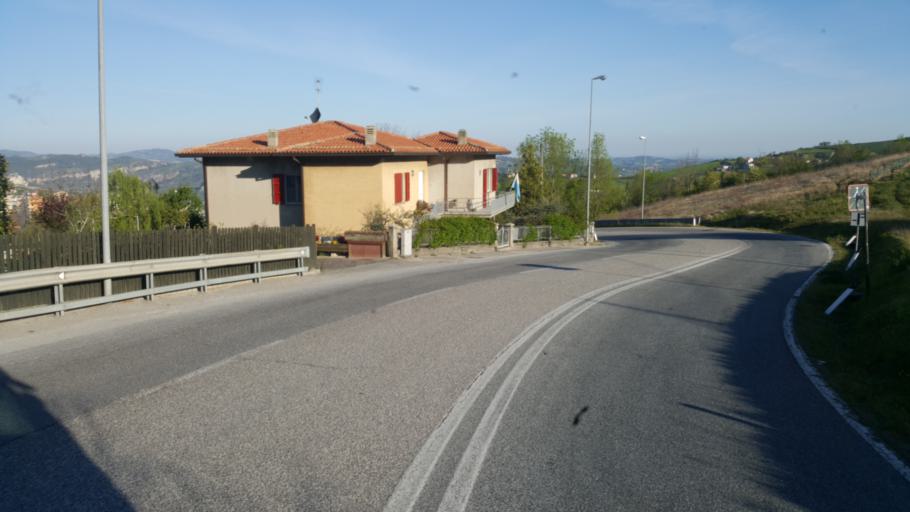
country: SM
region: Borgo Maggiore
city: Borgo Maggiore
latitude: 43.9448
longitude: 12.4373
